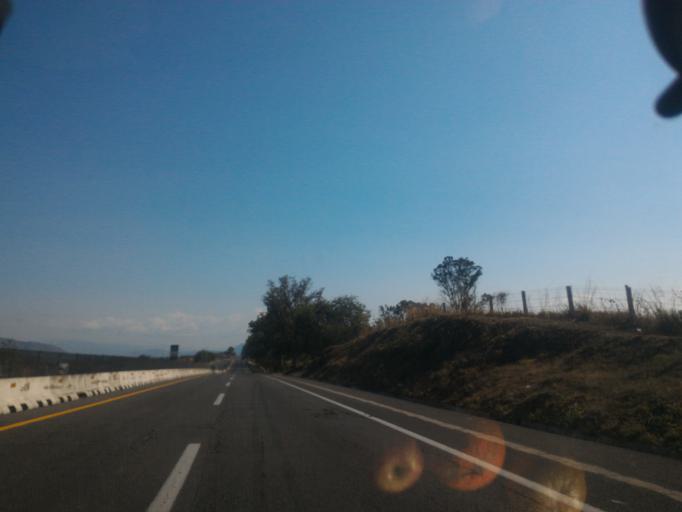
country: MX
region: Jalisco
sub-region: Zapotlan el Grande
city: Ciudad Guzman [CERESO]
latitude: 19.6317
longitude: -103.4662
